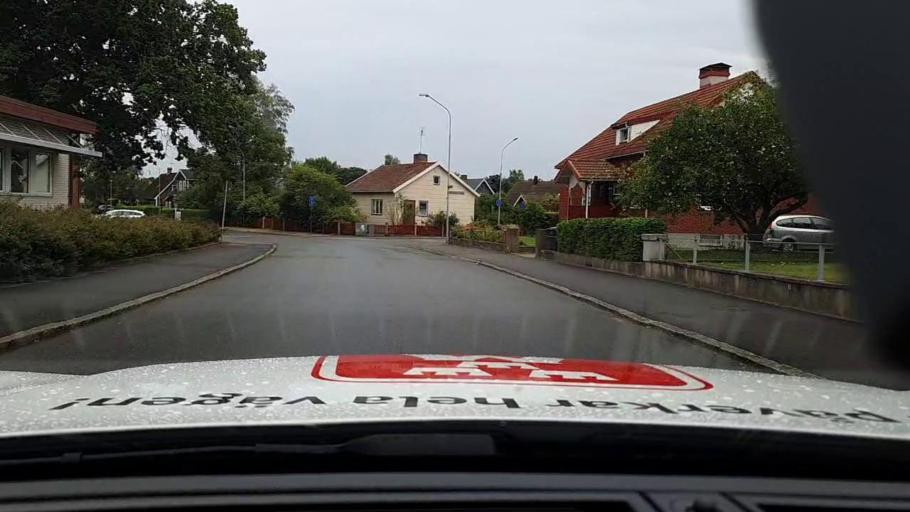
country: SE
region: Skane
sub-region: Hassleholms Kommun
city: Hassleholm
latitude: 56.1655
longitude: 13.7741
